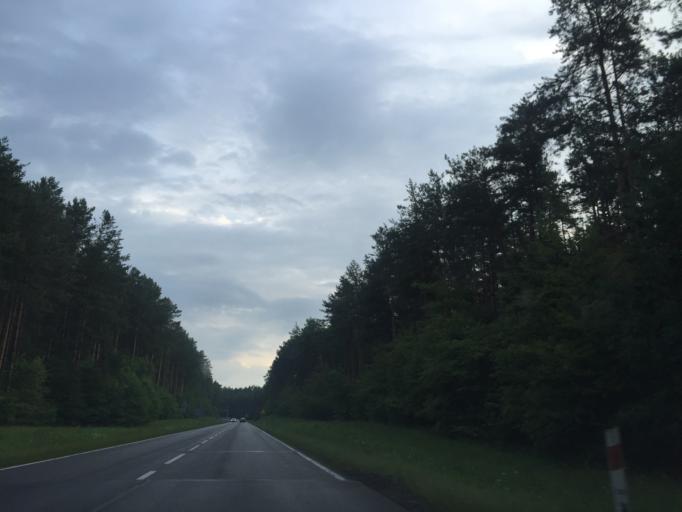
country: PL
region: Masovian Voivodeship
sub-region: Powiat ostrowski
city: Ostrow Mazowiecka
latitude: 52.7783
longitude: 21.8635
